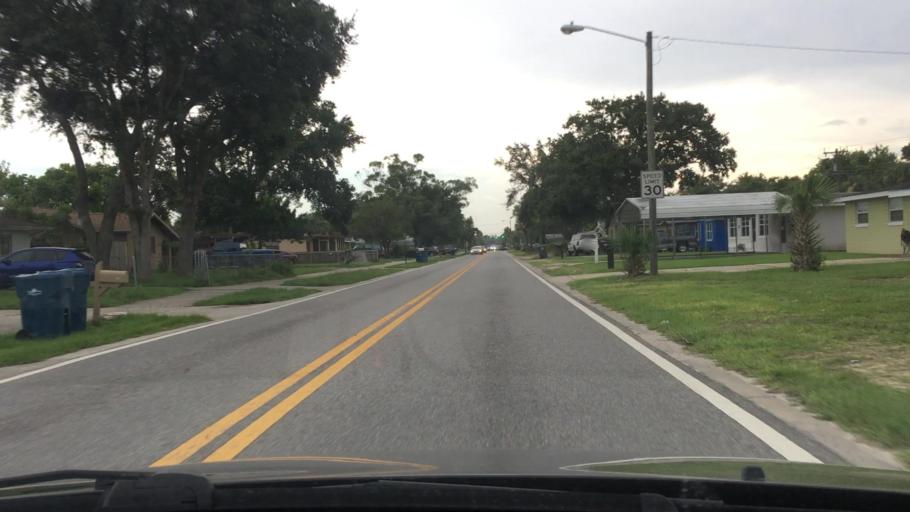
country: US
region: Florida
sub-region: Volusia County
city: Holly Hill
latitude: 29.2285
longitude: -81.0624
